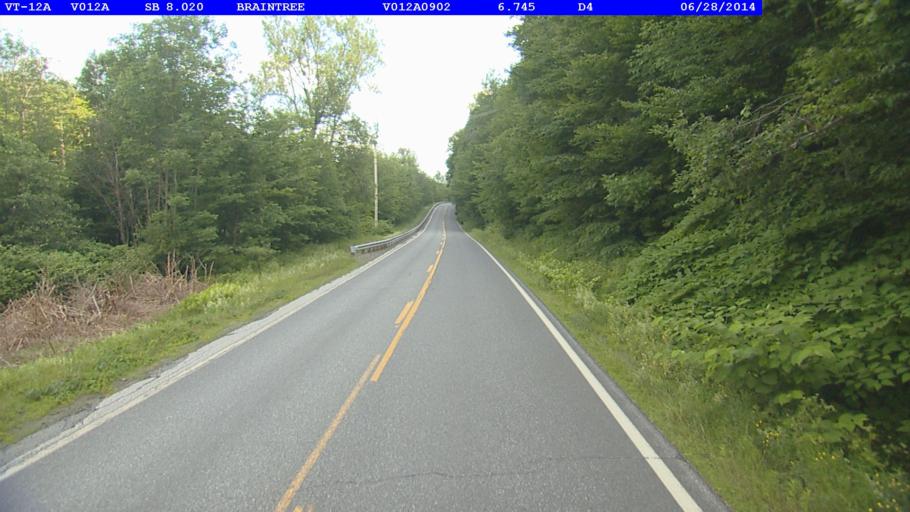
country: US
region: Vermont
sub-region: Orange County
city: Randolph
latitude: 44.0043
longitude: -72.7540
